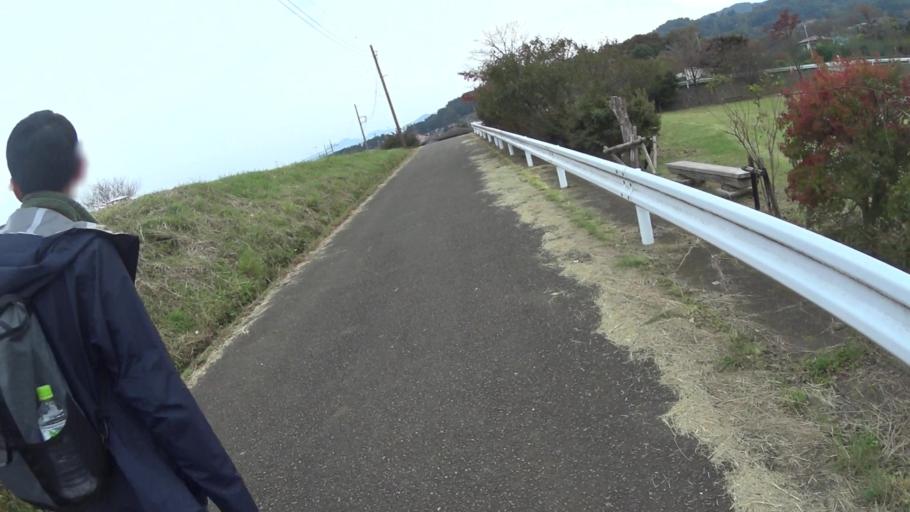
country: JP
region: Kanagawa
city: Hadano
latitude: 35.3935
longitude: 139.2236
